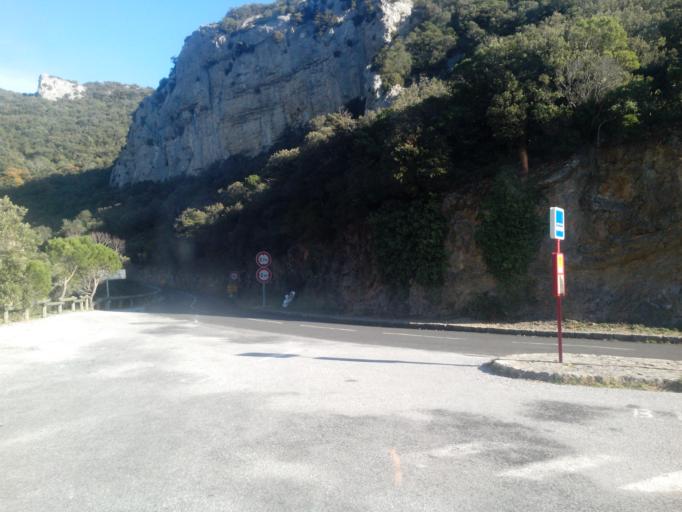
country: FR
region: Languedoc-Roussillon
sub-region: Departement des Pyrenees-Orientales
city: Saint-Paul-de-Fenouillet
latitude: 42.8357
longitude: 2.4802
